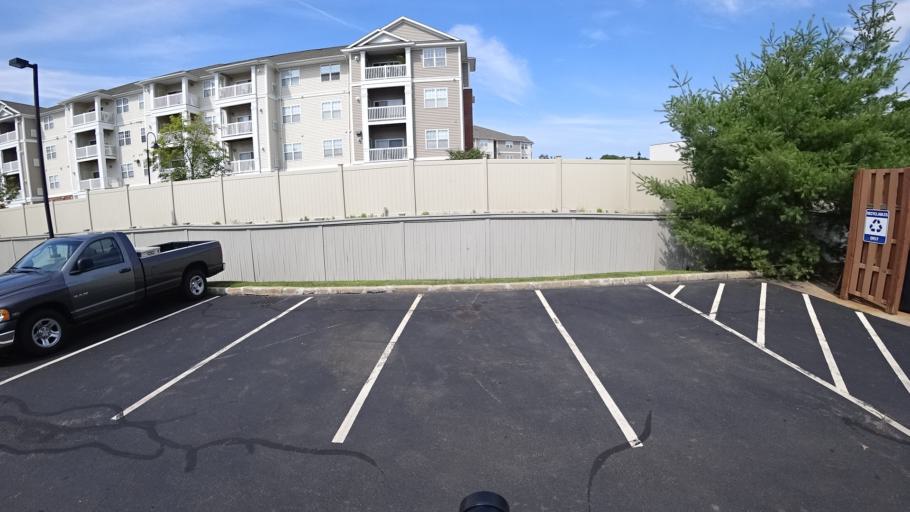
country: US
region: Massachusetts
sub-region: Norfolk County
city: Dedham
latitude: 42.2286
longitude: -71.1754
